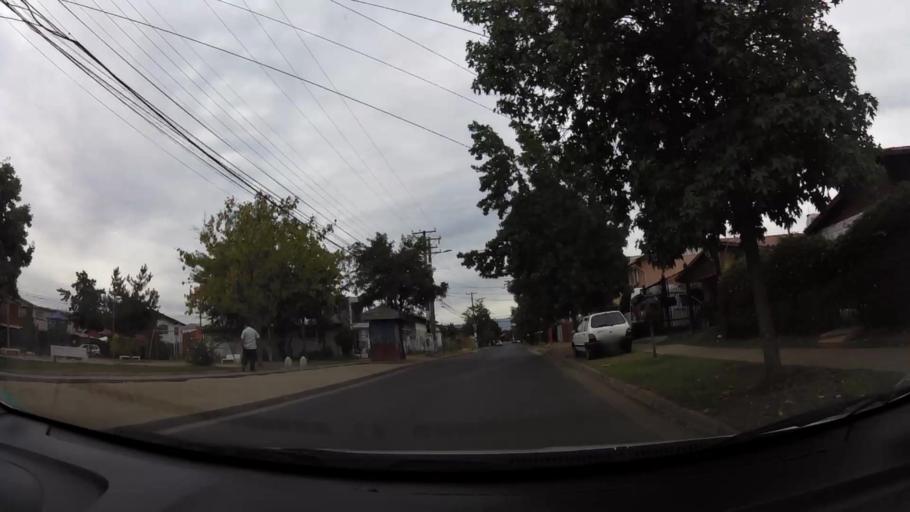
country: CL
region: O'Higgins
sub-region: Provincia de Cachapoal
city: Rancagua
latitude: -34.1297
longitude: -70.7371
